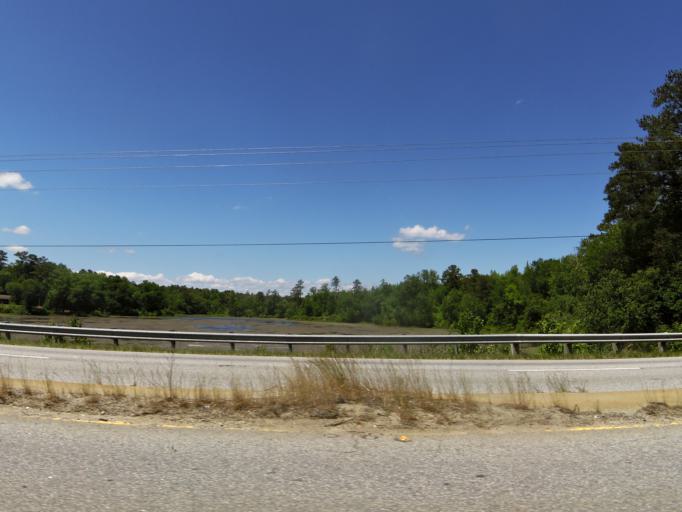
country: US
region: South Carolina
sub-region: Aiken County
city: Clearwater
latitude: 33.5053
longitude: -81.8938
